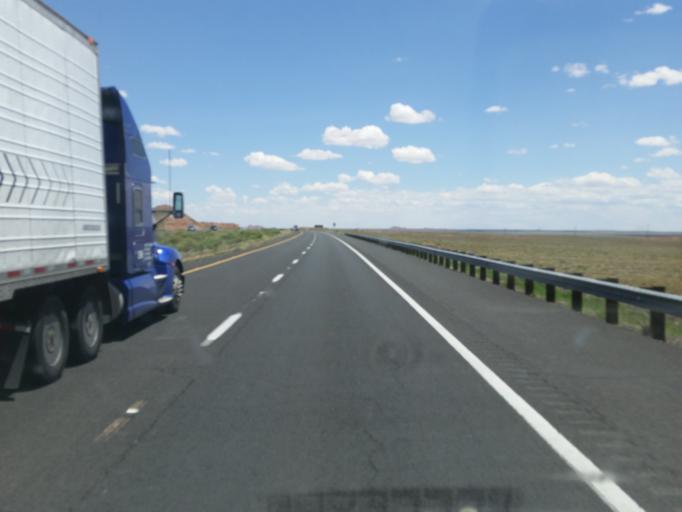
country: US
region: Arizona
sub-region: Navajo County
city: Joseph City
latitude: 34.9180
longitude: -110.2538
